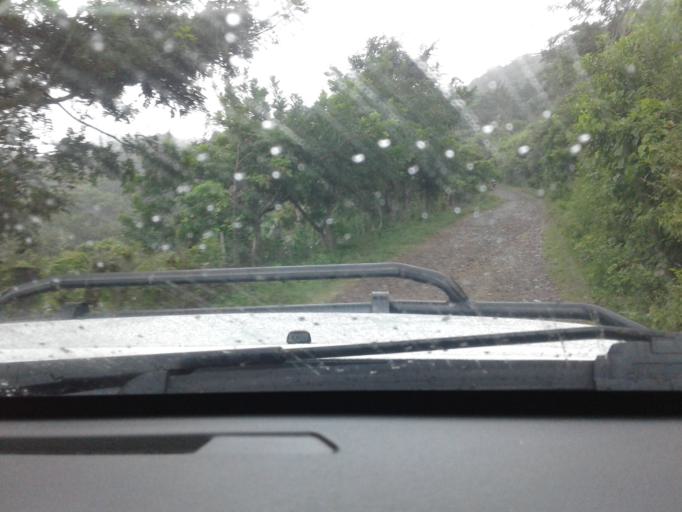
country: NI
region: Leon
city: Santa Rosa del Penon
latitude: 12.9014
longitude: -86.2380
